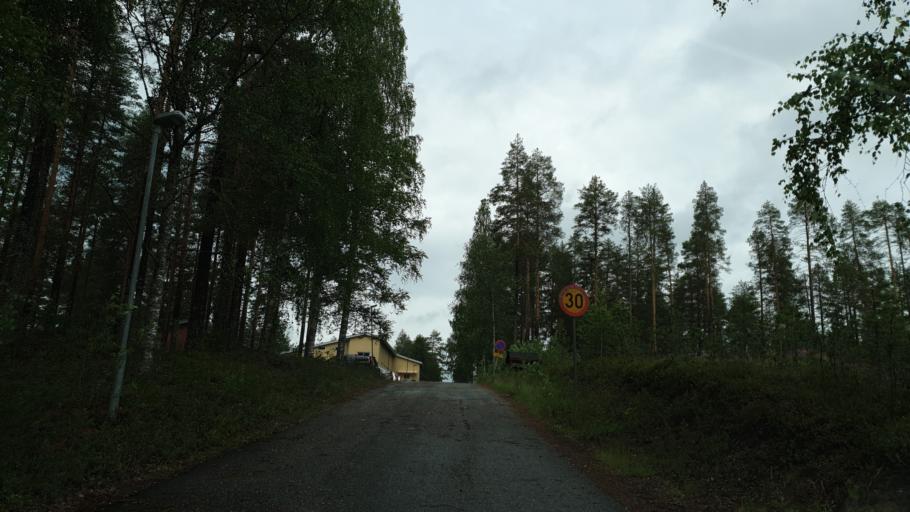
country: FI
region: Kainuu
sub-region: Kehys-Kainuu
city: Kuhmo
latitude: 64.0934
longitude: 29.4336
